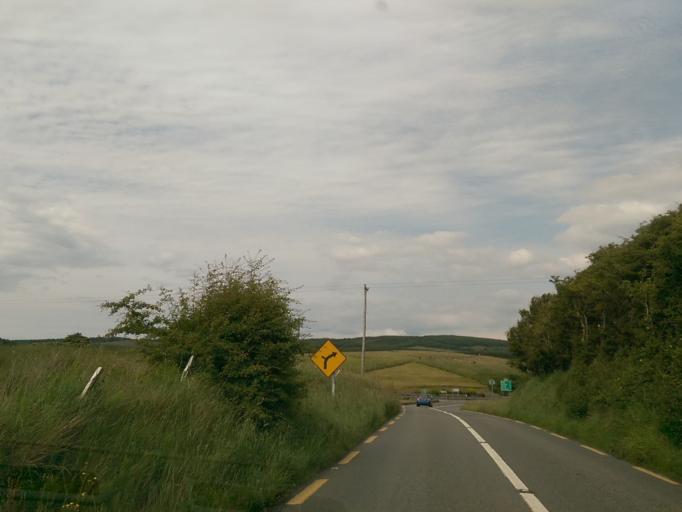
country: IE
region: Connaught
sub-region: County Galway
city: Bearna
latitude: 53.0370
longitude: -9.2861
